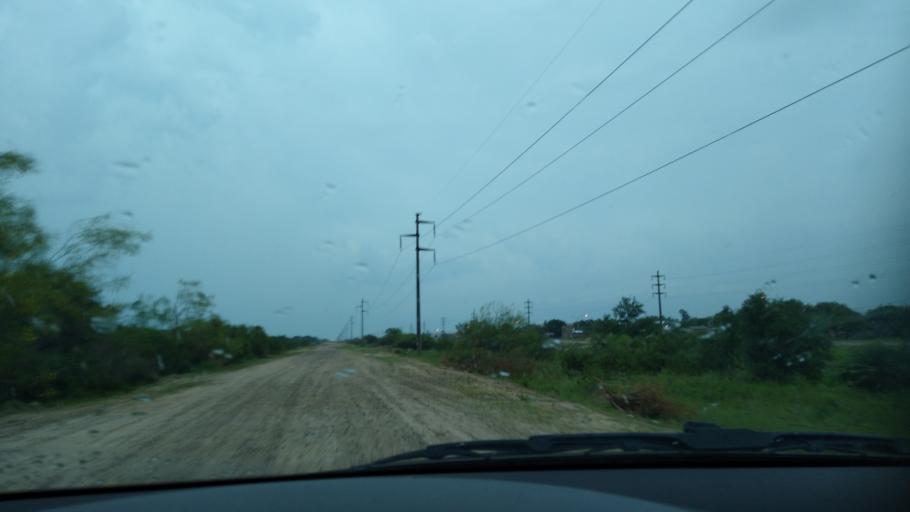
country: AR
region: Chaco
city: Puerto Vilelas
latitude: -27.5052
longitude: -58.9699
